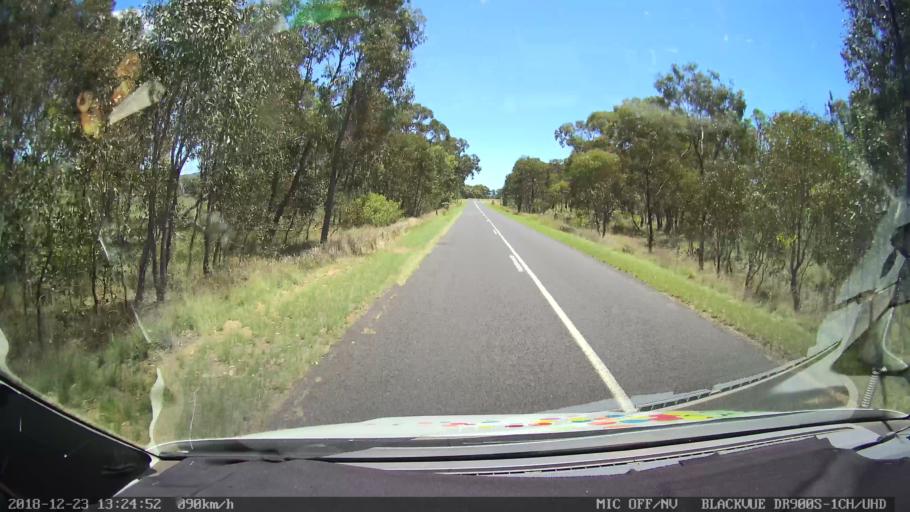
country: AU
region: New South Wales
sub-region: Armidale Dumaresq
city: Armidale
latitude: -30.4762
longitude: 151.3836
